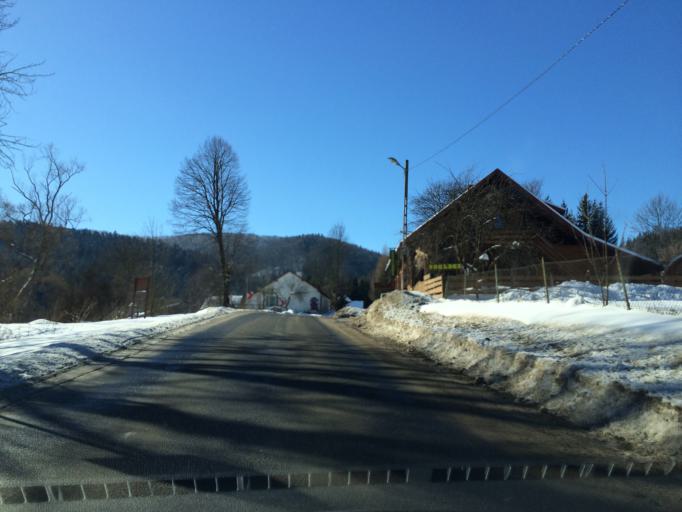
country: PL
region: Subcarpathian Voivodeship
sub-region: Powiat leski
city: Cisna
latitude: 49.2114
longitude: 22.3309
